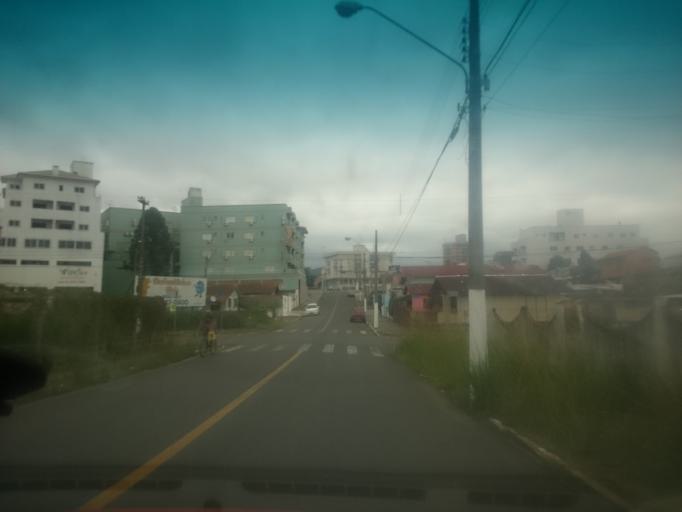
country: BR
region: Santa Catarina
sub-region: Lages
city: Lages
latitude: -27.8158
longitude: -50.3107
